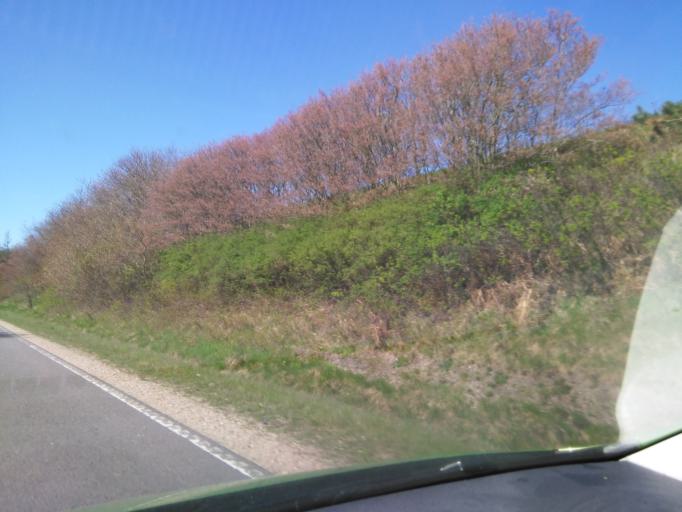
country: DK
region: South Denmark
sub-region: Varde Kommune
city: Oksbol
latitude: 55.6193
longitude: 8.2971
